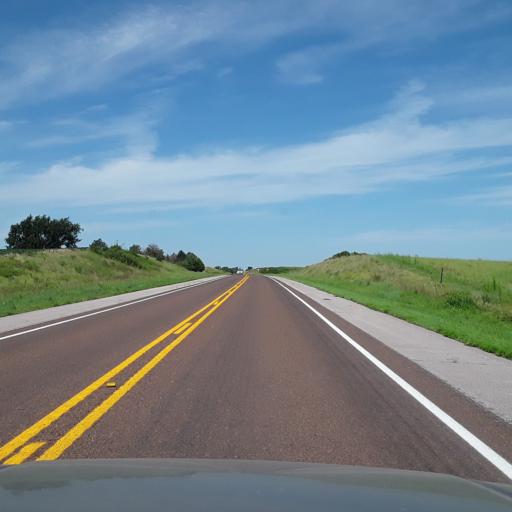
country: US
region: Nebraska
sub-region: Lancaster County
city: Lincoln
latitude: 40.8868
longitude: -96.8510
